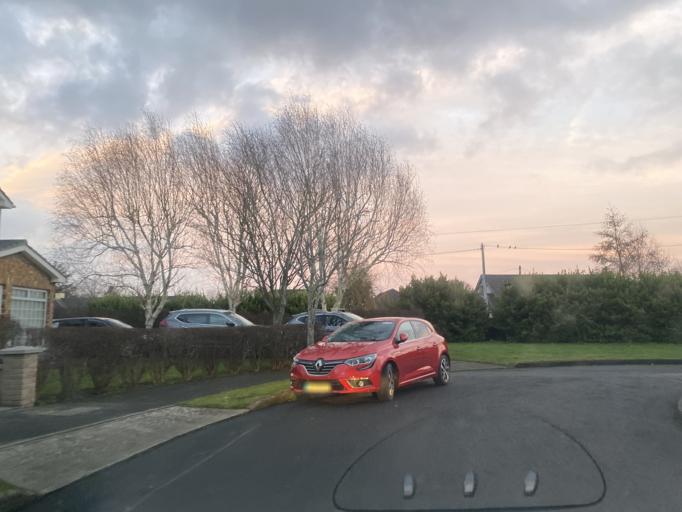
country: IE
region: Leinster
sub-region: Kildare
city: Celbridge
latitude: 53.3466
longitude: -6.5427
